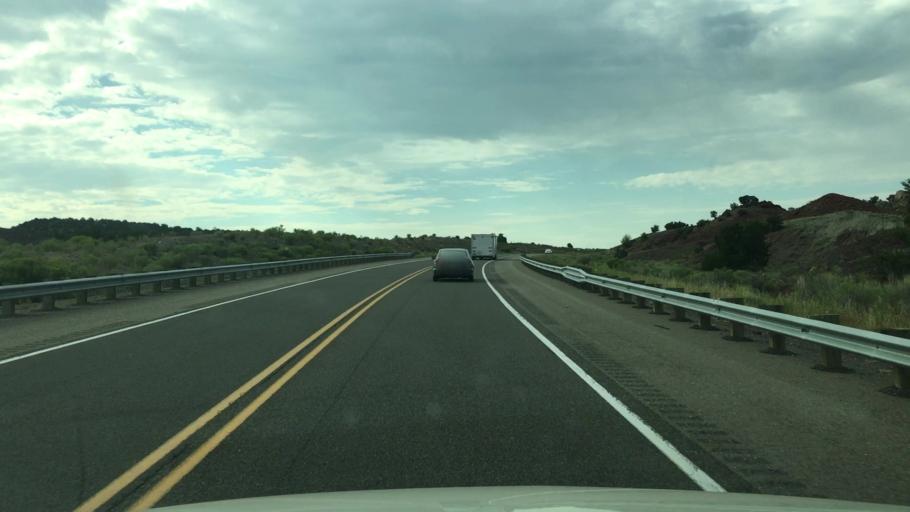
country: US
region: New Mexico
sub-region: Santa Fe County
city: Eldorado at Santa Fe
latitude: 35.2720
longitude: -105.8111
